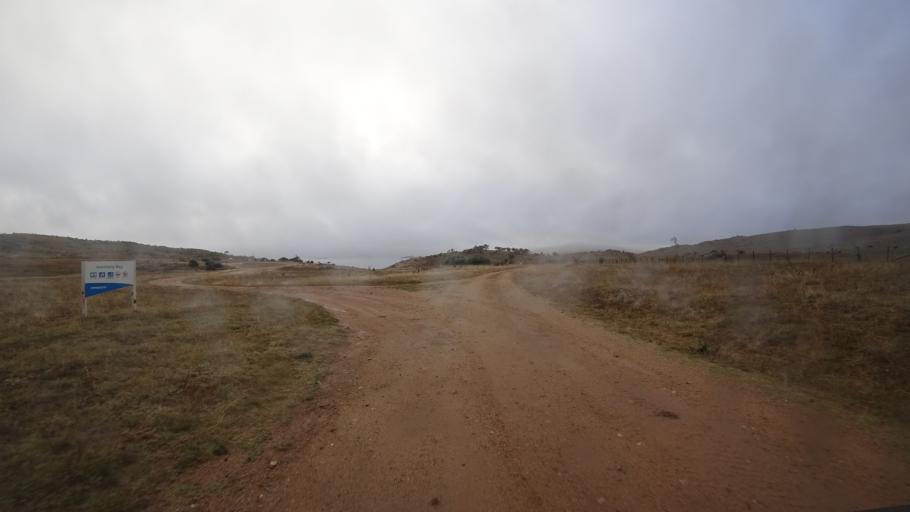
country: AU
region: New South Wales
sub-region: Snowy River
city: Jindabyne
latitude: -36.3868
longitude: 148.6046
